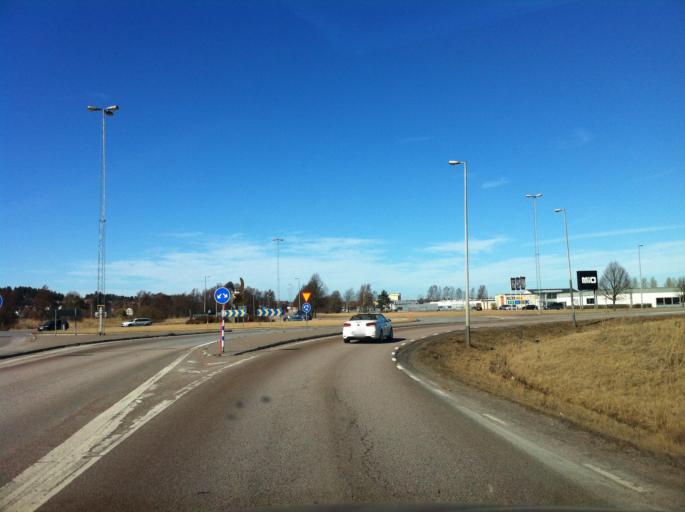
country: SE
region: Vaestra Goetaland
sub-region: Gullspangs Kommun
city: Gullspang
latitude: 58.9133
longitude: 14.1140
